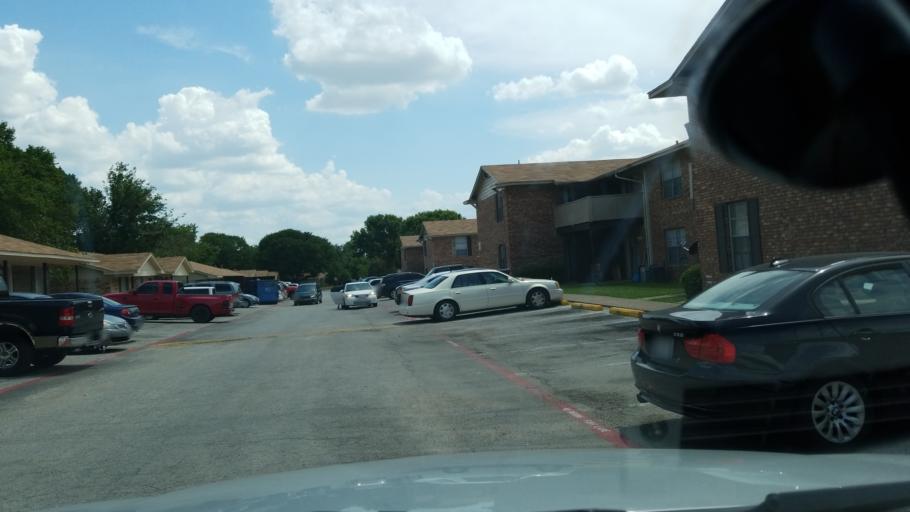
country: US
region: Texas
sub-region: Dallas County
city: Irving
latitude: 32.8275
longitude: -96.9819
